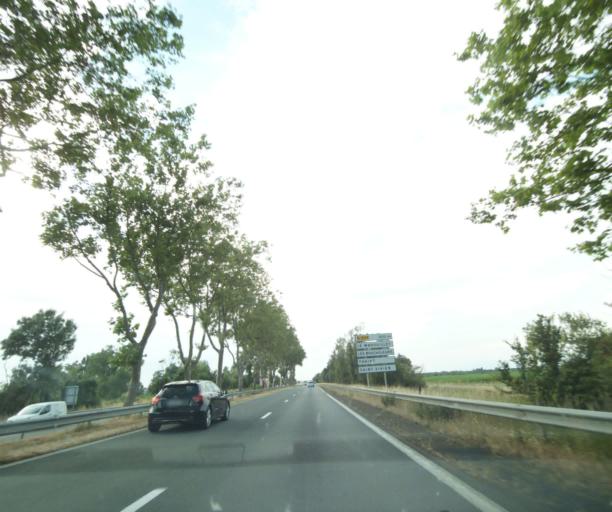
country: FR
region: Poitou-Charentes
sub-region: Departement de la Charente-Maritime
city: Yves
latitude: 46.0538
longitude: -1.0544
